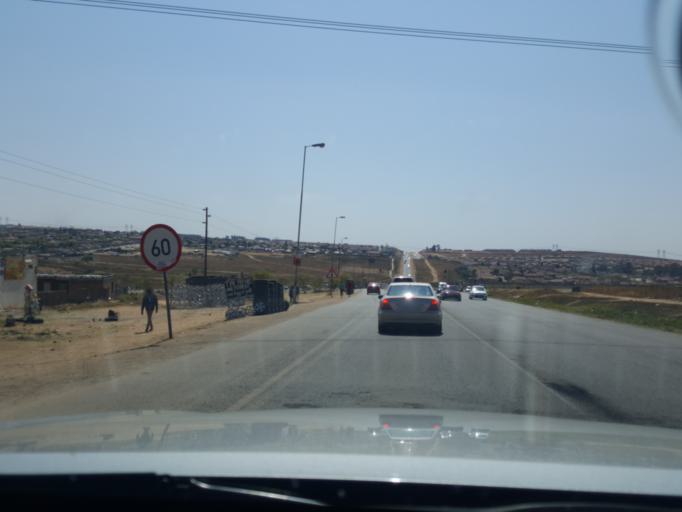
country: ZA
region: Gauteng
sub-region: City of Johannesburg Metropolitan Municipality
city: Midrand
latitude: -25.9203
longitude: 28.0991
